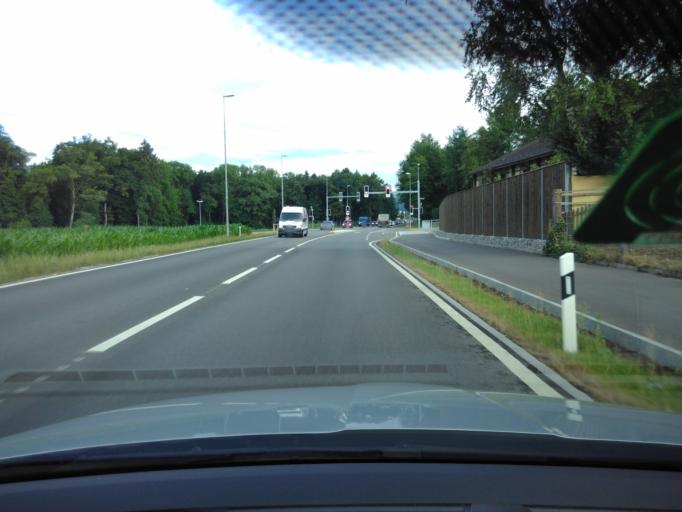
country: CH
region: Zurich
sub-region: Bezirk Dielsdorf
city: Regensdorf
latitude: 47.4318
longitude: 8.4836
